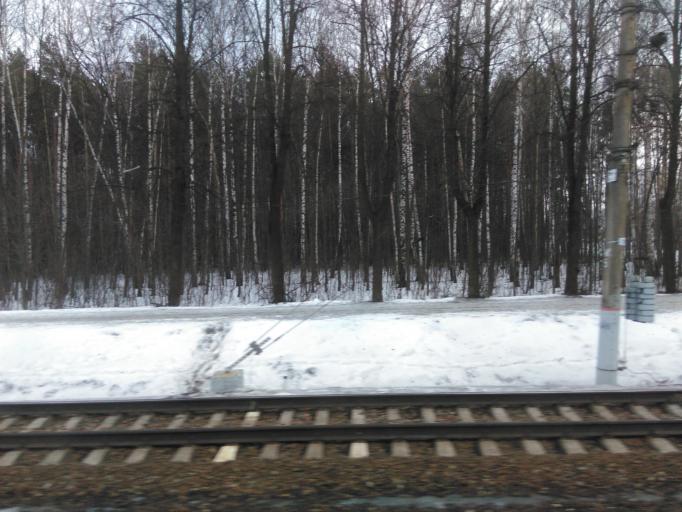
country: RU
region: Moskovskaya
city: Mytishchi
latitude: 55.9264
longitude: 37.7755
